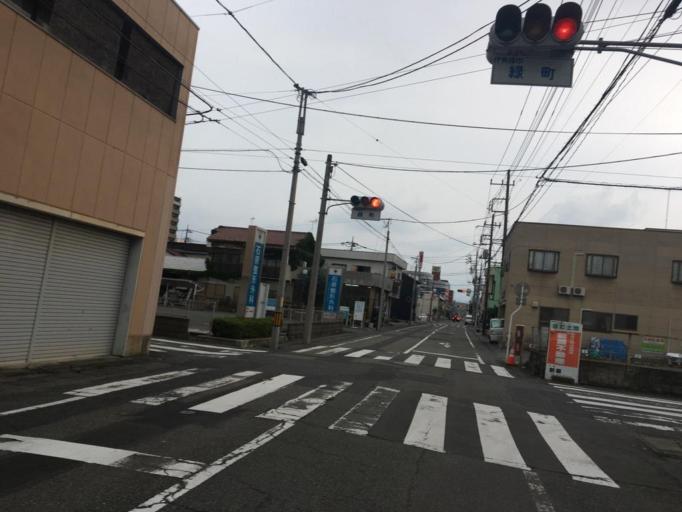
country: JP
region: Gunma
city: Isesaki
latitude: 36.3186
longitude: 139.1960
